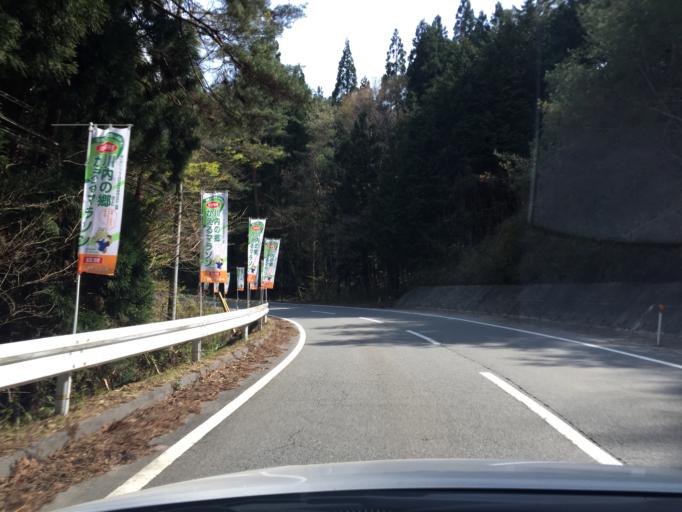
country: JP
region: Fukushima
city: Namie
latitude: 37.3024
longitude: 140.8359
